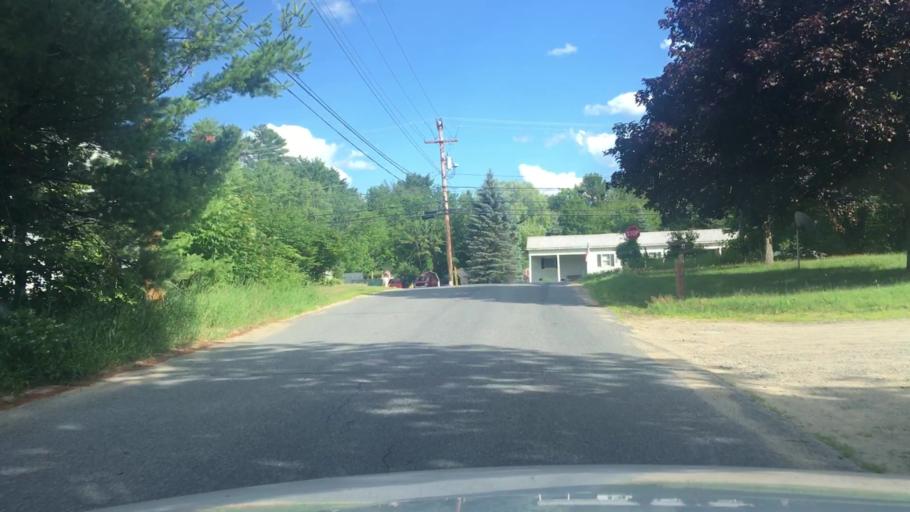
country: US
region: Maine
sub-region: Franklin County
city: Wilton
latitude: 44.5982
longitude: -70.2191
